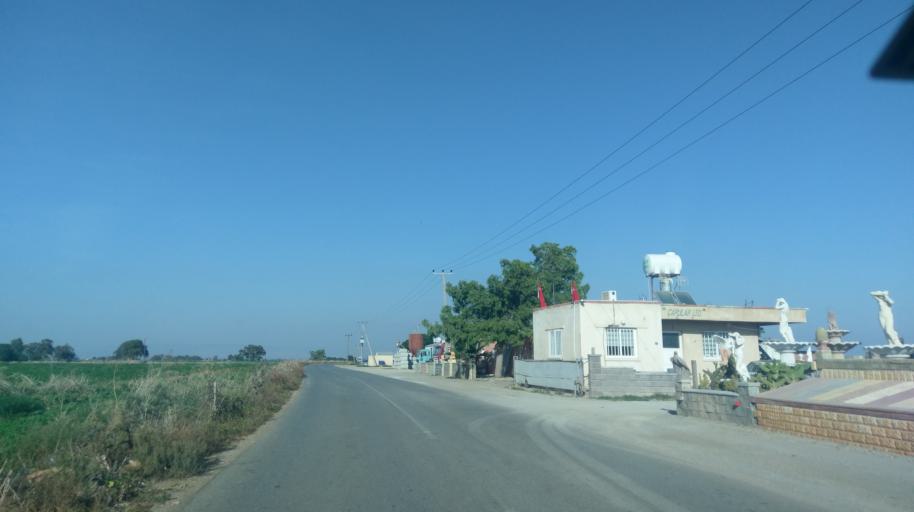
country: CY
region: Larnaka
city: Pergamos
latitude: 35.0602
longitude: 33.7127
